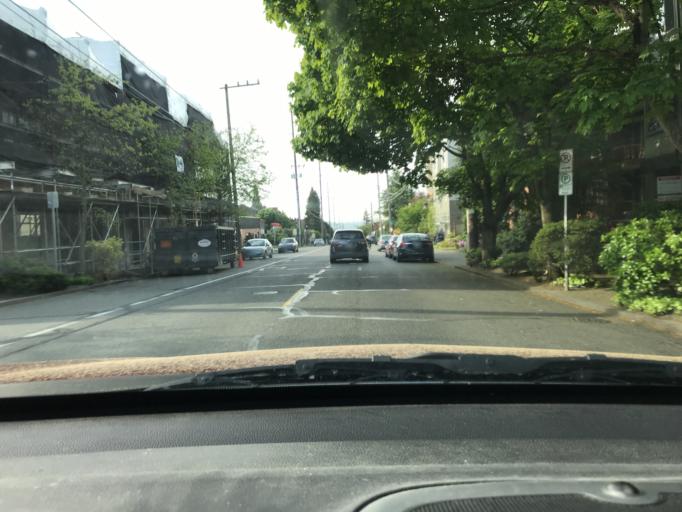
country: US
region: Washington
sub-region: King County
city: Shoreline
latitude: 47.6898
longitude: -122.3231
